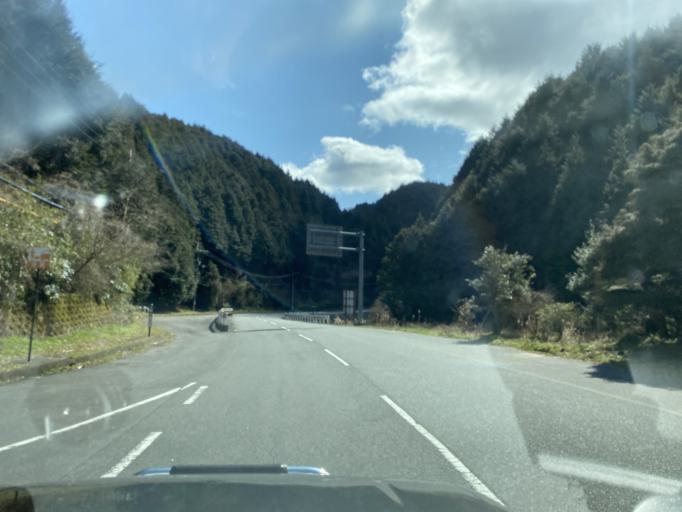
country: JP
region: Nara
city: Nara-shi
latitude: 34.6906
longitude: 135.9510
